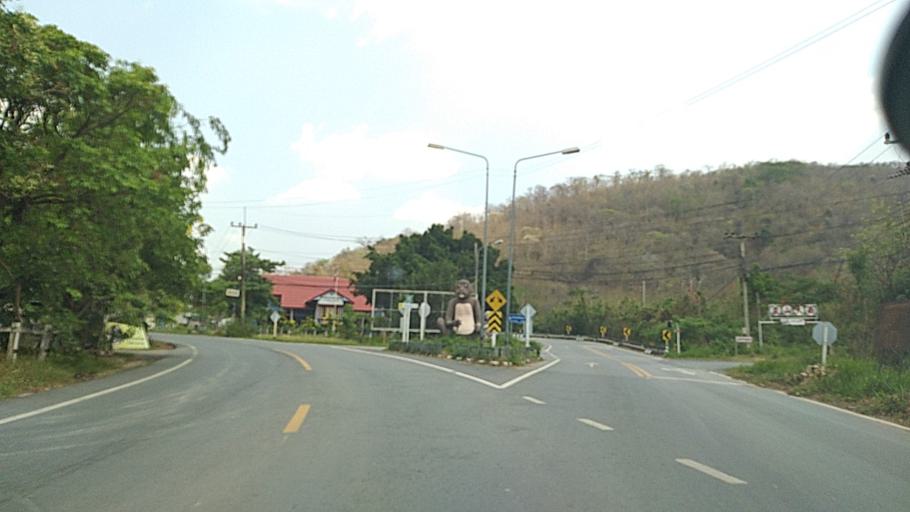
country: TH
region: Sara Buri
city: Saraburi
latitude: 14.4576
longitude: 100.9462
